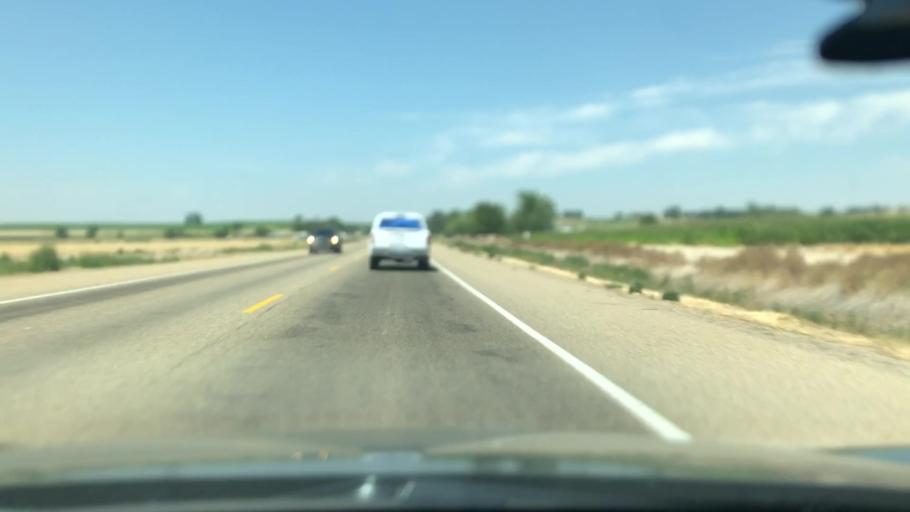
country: US
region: Idaho
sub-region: Canyon County
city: Parma
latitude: 43.8104
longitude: -116.9543
